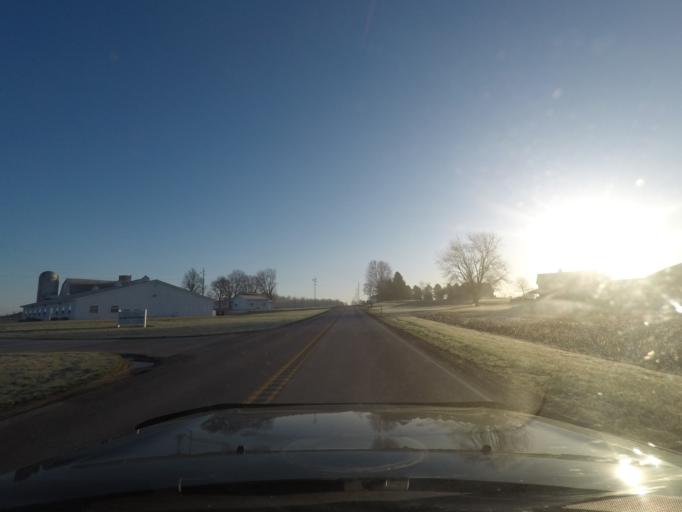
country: US
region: Indiana
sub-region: Elkhart County
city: Wakarusa
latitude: 41.5357
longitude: -85.9415
